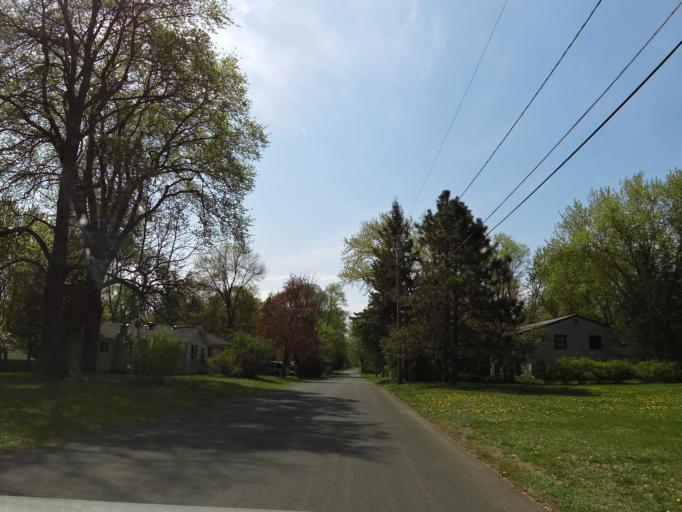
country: US
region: Minnesota
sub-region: Washington County
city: Lake Saint Croix Beach
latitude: 44.9263
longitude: -92.7676
